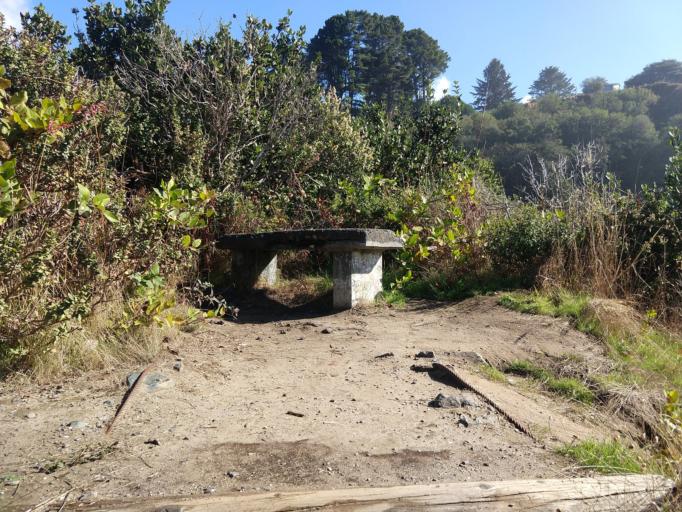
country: US
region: California
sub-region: Humboldt County
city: Westhaven-Moonstone
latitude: 41.0359
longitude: -124.1185
